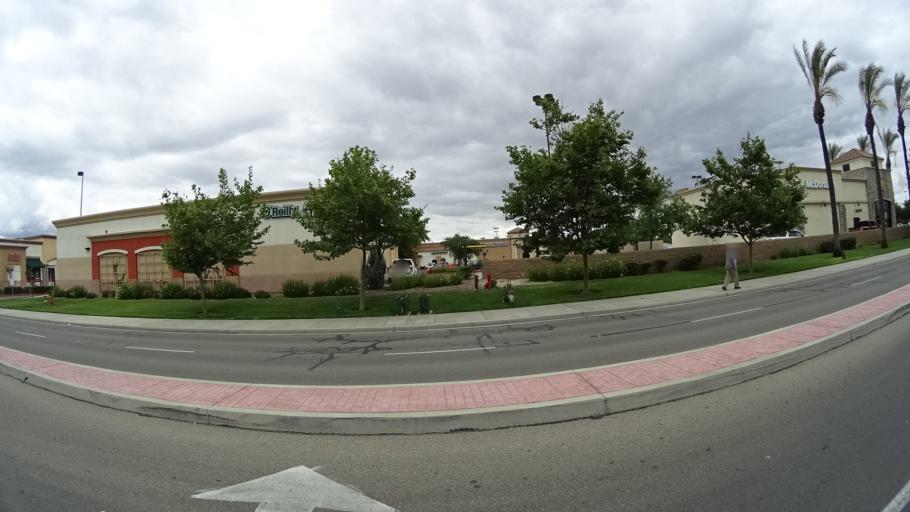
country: US
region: California
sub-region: Kings County
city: Hanford
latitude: 36.3228
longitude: -119.6739
